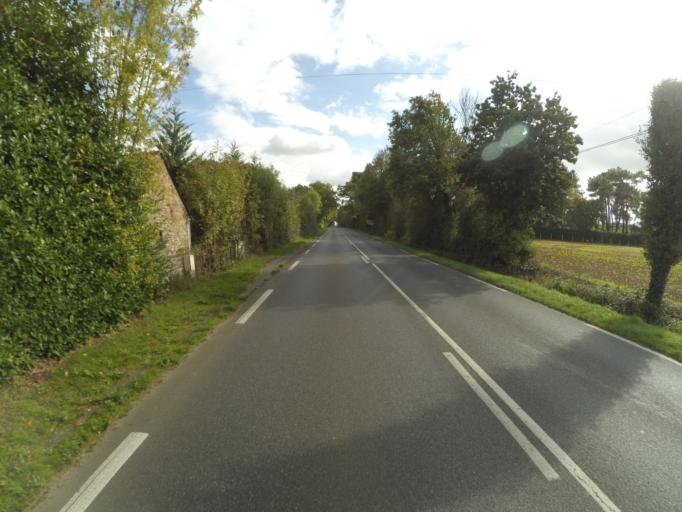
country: FR
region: Pays de la Loire
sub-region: Departement de la Loire-Atlantique
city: Saint-Nicolas-de-Redon
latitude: 47.6257
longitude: -2.0469
